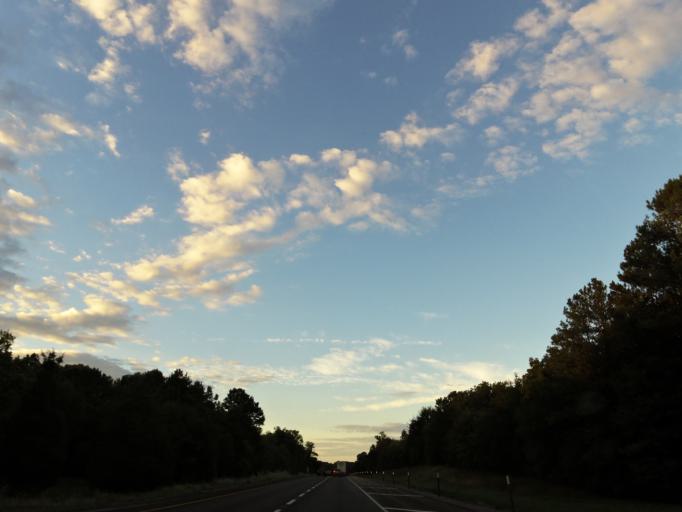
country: US
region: Tennessee
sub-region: Bradley County
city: Hopewell
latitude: 35.3390
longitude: -84.7523
